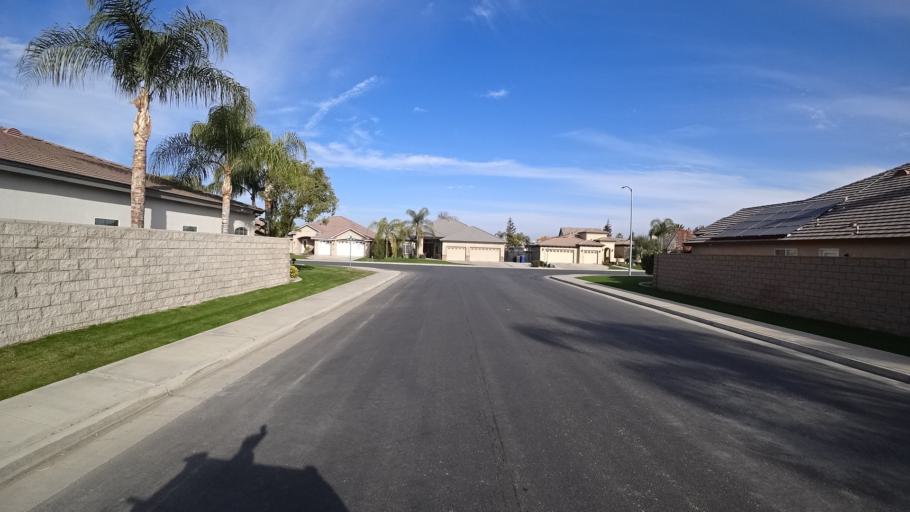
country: US
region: California
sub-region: Kern County
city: Rosedale
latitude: 35.4081
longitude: -119.1432
